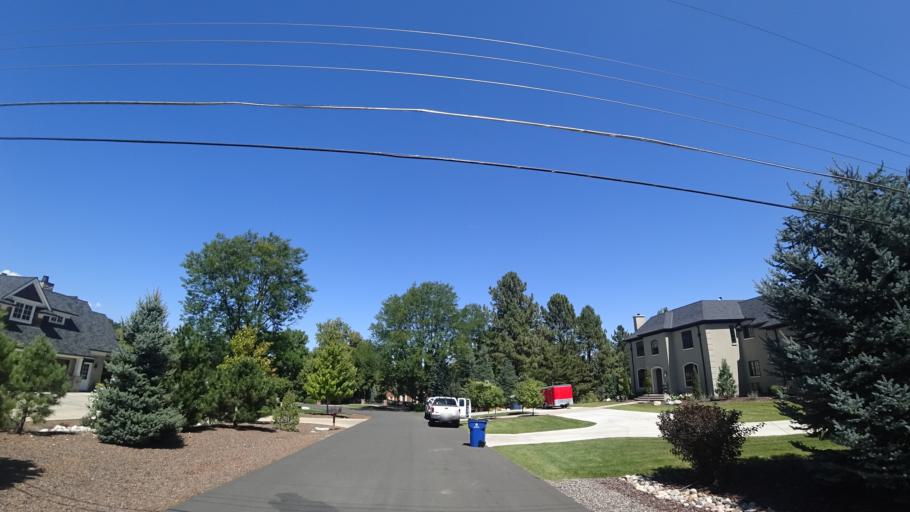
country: US
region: Colorado
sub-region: Arapahoe County
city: Cherry Hills Village
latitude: 39.6326
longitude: -104.9525
